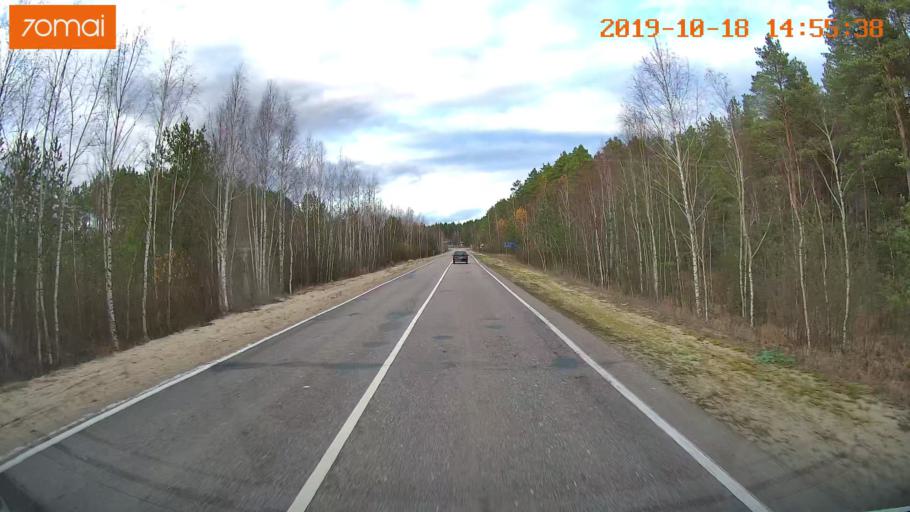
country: RU
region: Vladimir
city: Kurlovo
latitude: 55.4551
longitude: 40.5892
